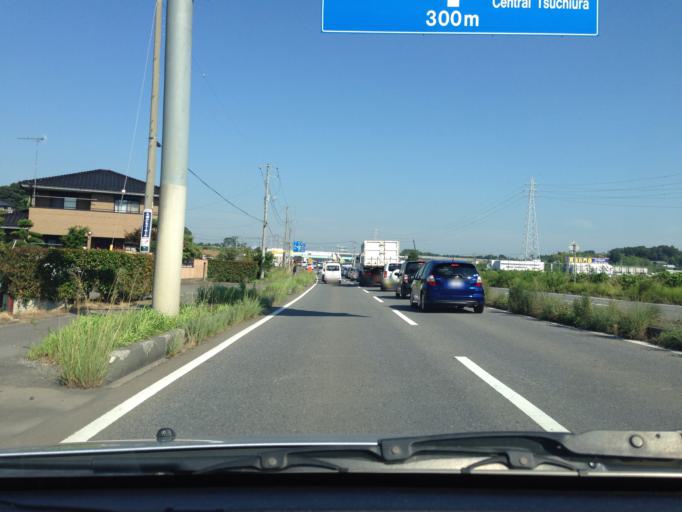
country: JP
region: Ibaraki
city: Naka
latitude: 36.0549
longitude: 140.1798
